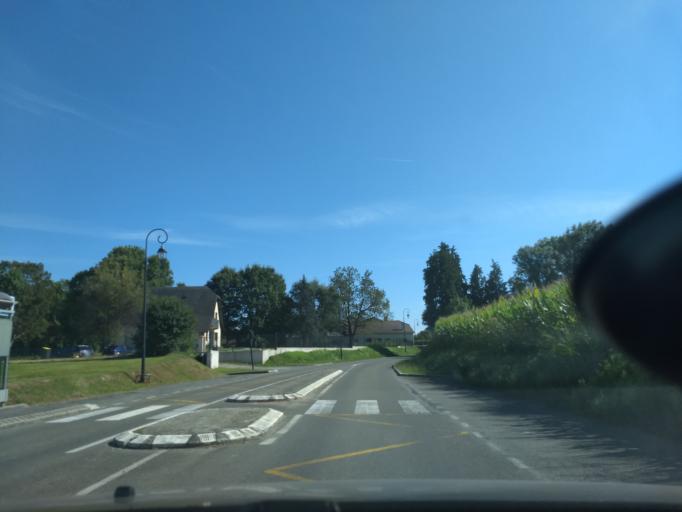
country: FR
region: Aquitaine
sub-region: Departement des Pyrenees-Atlantiques
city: Soumoulou
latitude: 43.2760
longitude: -0.1827
